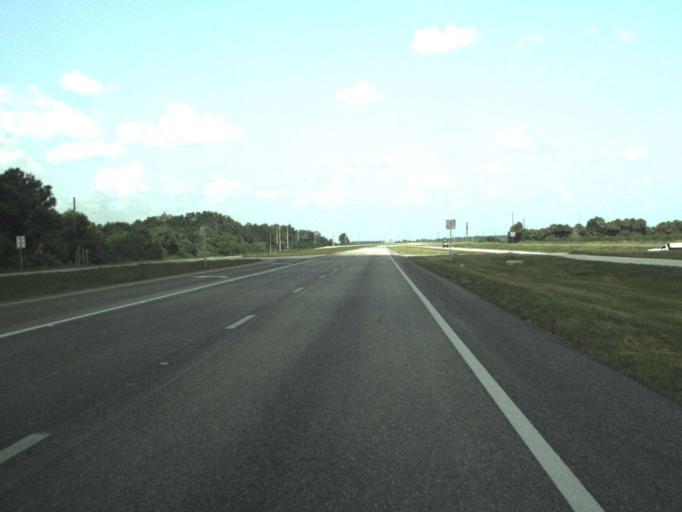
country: US
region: Florida
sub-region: Saint Lucie County
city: Fort Pierce South
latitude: 27.3683
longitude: -80.5494
